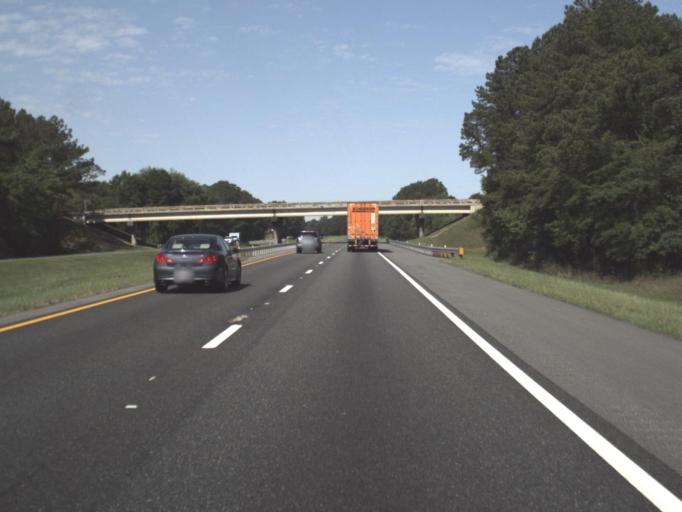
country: US
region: Florida
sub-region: Holmes County
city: Bonifay
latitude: 30.7529
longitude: -85.8496
